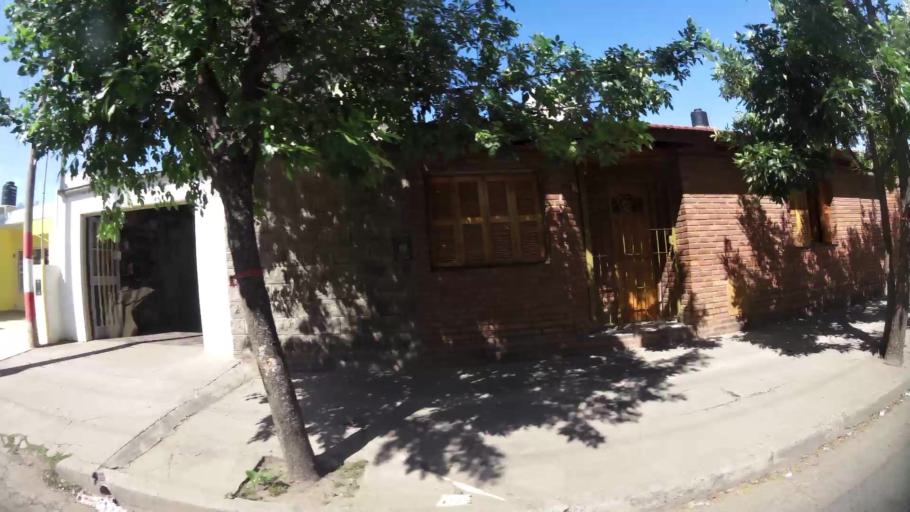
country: AR
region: Cordoba
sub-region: Departamento de Capital
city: Cordoba
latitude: -31.3734
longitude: -64.1723
